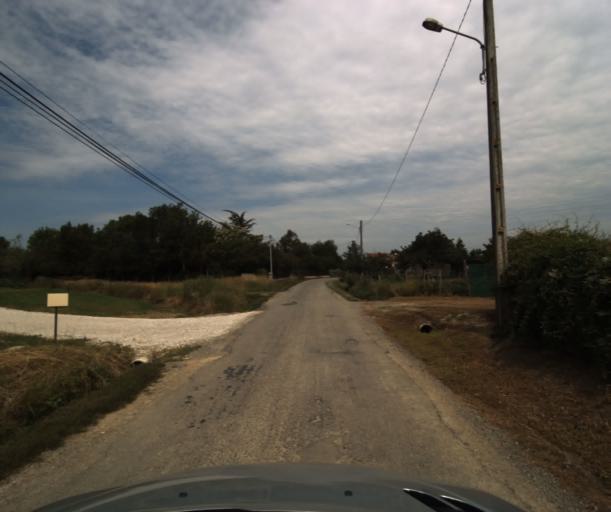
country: FR
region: Midi-Pyrenees
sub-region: Departement de la Haute-Garonne
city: Lacasse
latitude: 43.4162
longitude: 1.2711
